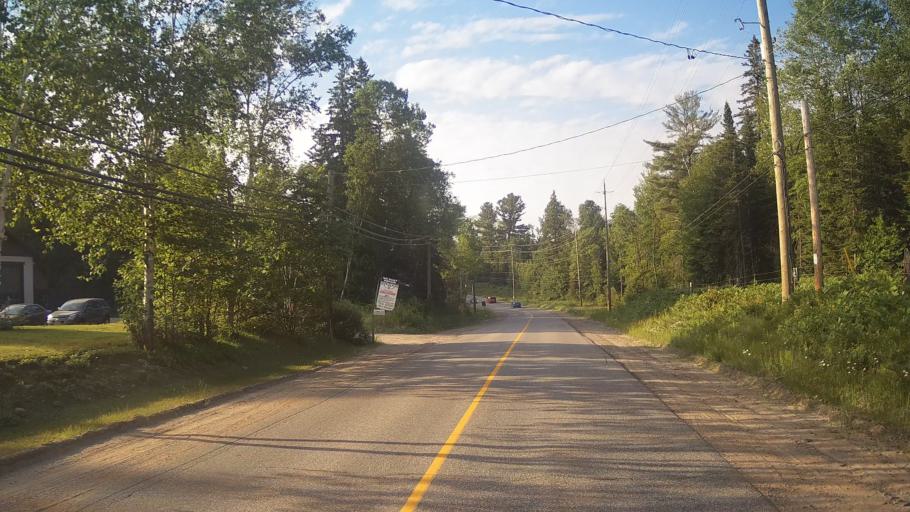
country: CA
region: Ontario
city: Huntsville
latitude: 45.3663
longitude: -79.2048
